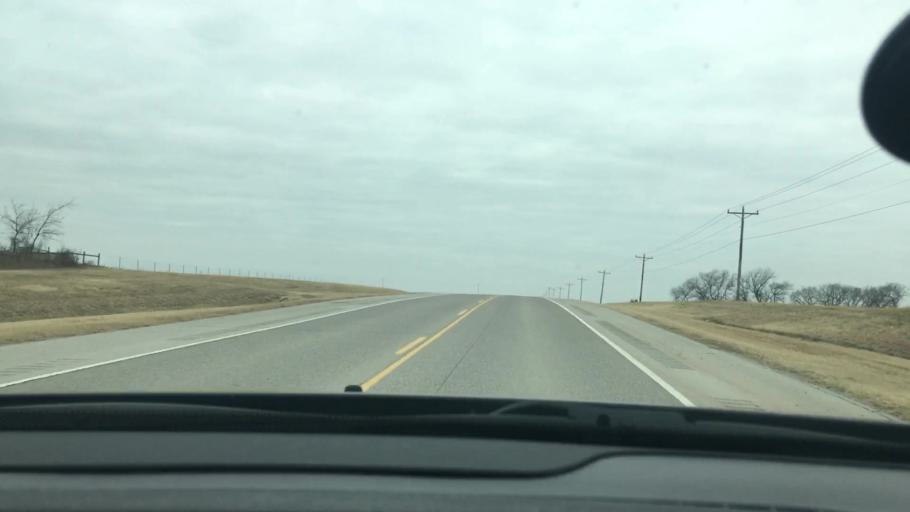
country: US
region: Oklahoma
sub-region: Murray County
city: Davis
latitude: 34.5214
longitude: -97.2905
